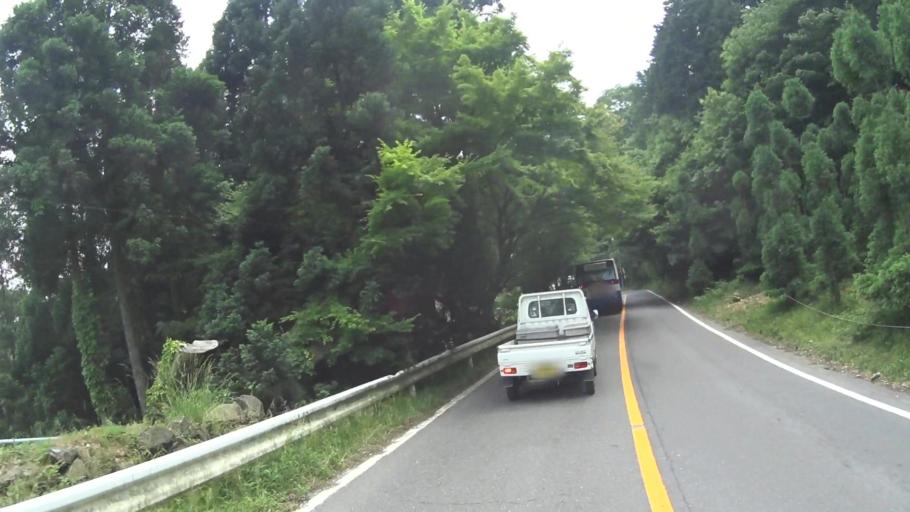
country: JP
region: Kyoto
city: Kyoto
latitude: 35.0481
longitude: 135.6803
